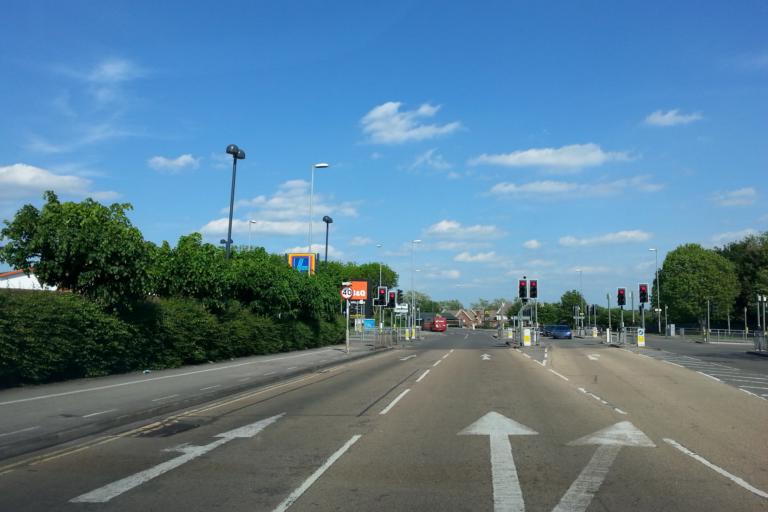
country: GB
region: England
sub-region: Nottinghamshire
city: Sutton in Ashfield
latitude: 53.1316
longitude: -1.2381
